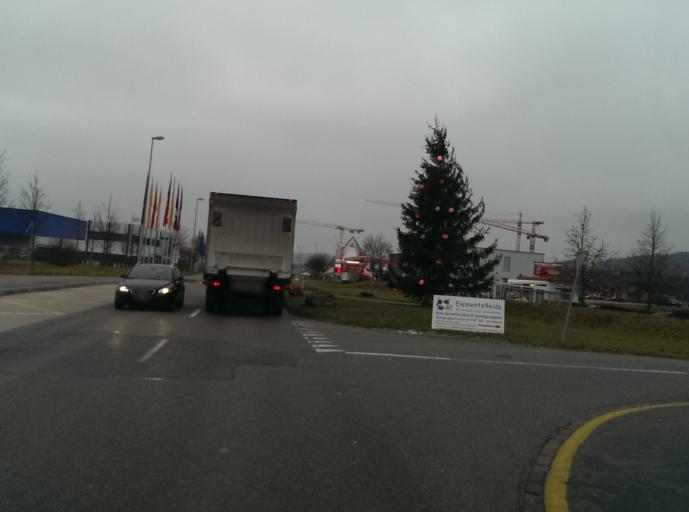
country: CH
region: Aargau
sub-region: Bezirk Baden
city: Spreitenbach
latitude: 47.4206
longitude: 8.3748
